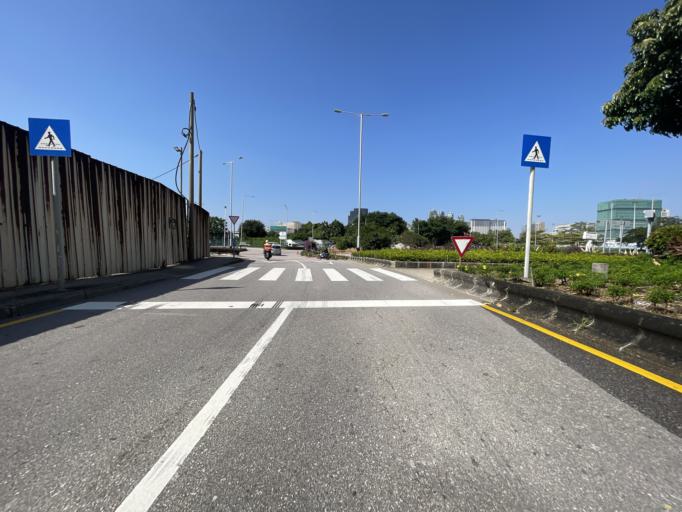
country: MO
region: Macau
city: Macau
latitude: 22.1309
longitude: 113.5591
